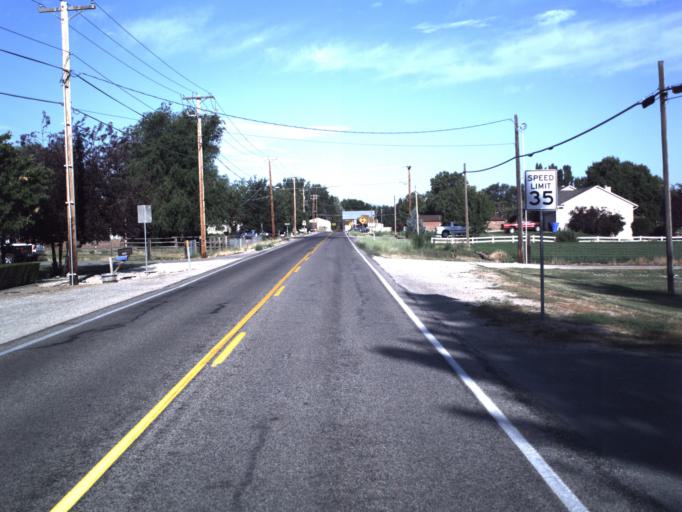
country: US
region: Utah
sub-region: Weber County
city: Plain City
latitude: 41.3054
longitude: -112.0769
